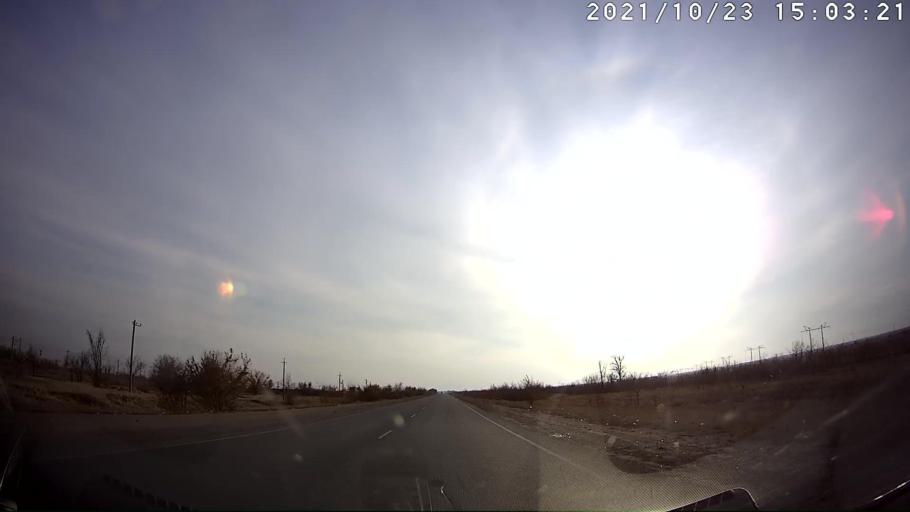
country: RU
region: Volgograd
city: Volgograd
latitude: 48.4140
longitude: 44.3775
